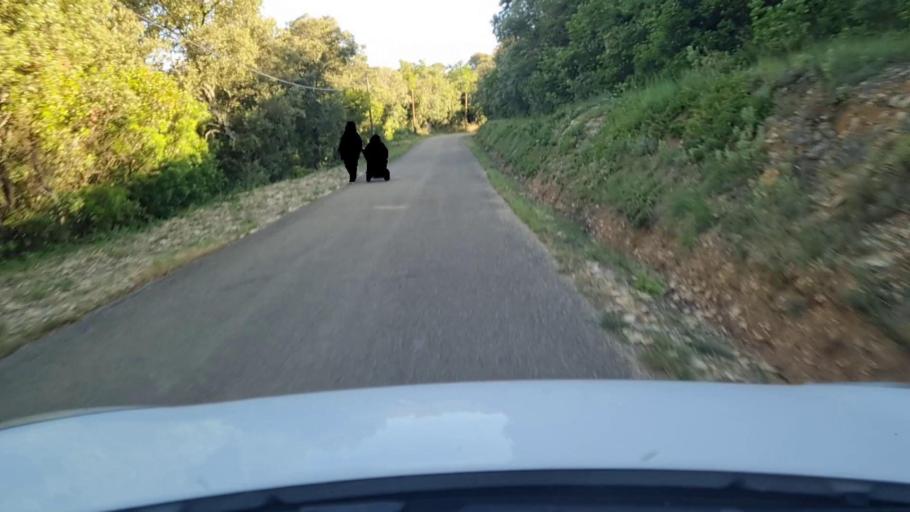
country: FR
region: Languedoc-Roussillon
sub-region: Departement du Gard
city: Villevieille
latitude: 43.8507
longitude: 4.0795
